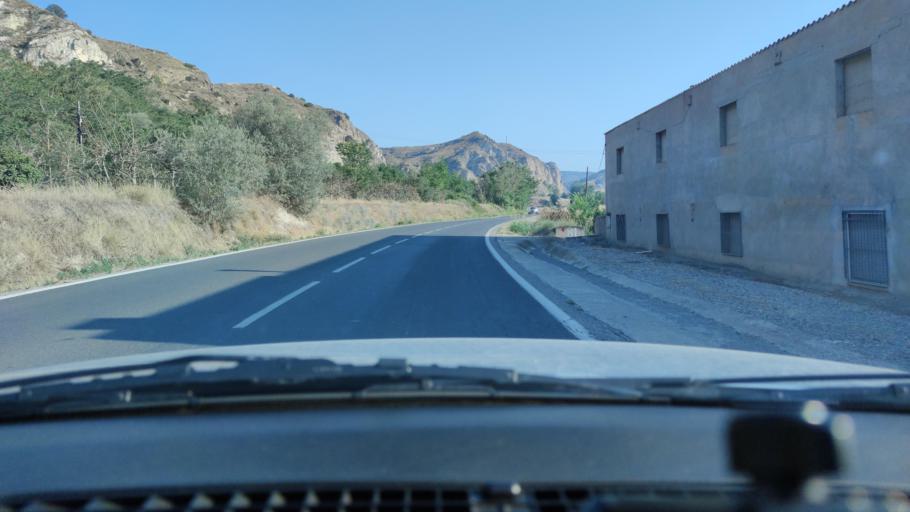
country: ES
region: Catalonia
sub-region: Provincia de Lleida
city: Balaguer
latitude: 41.8100
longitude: 0.8050
